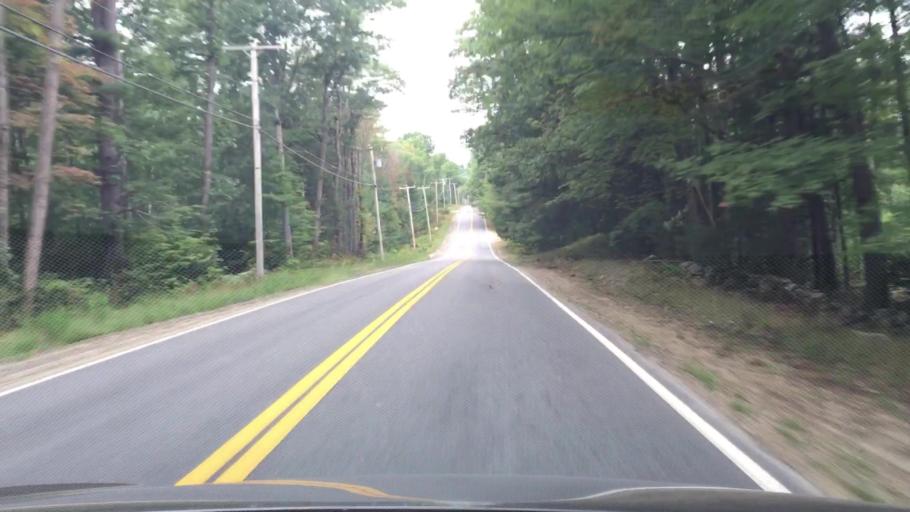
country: US
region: Maine
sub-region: Androscoggin County
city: Livermore
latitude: 44.3342
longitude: -70.2252
